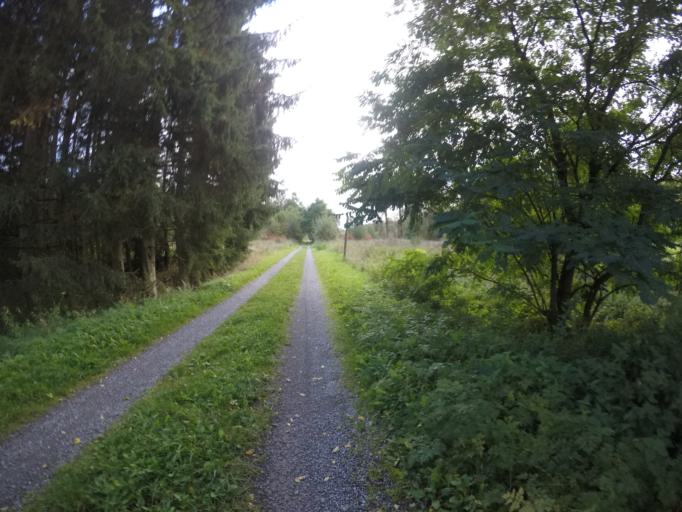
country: BE
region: Wallonia
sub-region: Province du Luxembourg
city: Fauvillers
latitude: 49.9203
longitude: 5.6927
